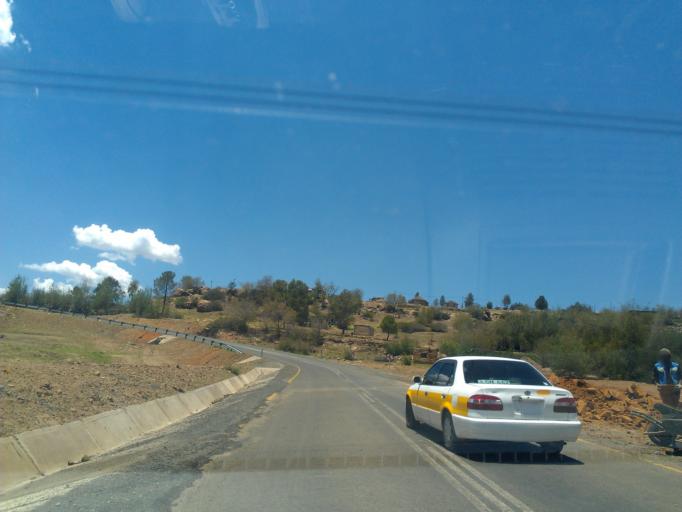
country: LS
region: Leribe
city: Maputsoe
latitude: -29.0921
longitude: 27.9576
